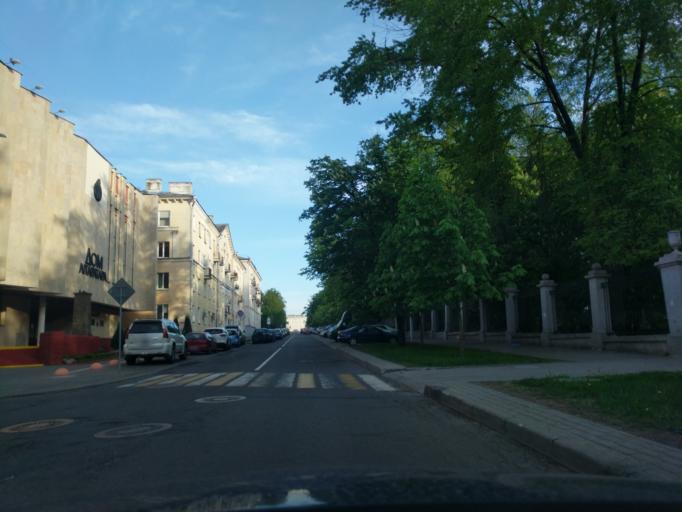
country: BY
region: Minsk
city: Minsk
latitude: 53.9062
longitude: 27.5739
